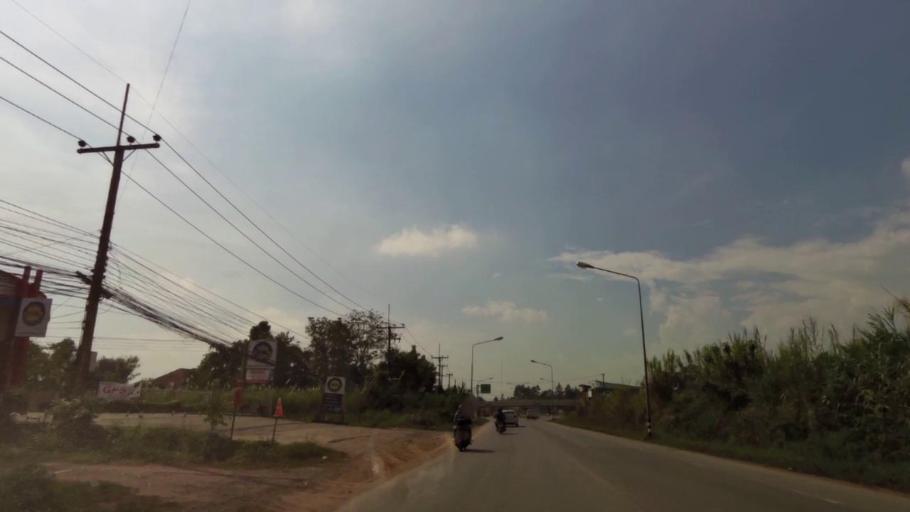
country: TH
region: Chiang Rai
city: Chiang Rai
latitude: 19.8772
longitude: 99.7884
